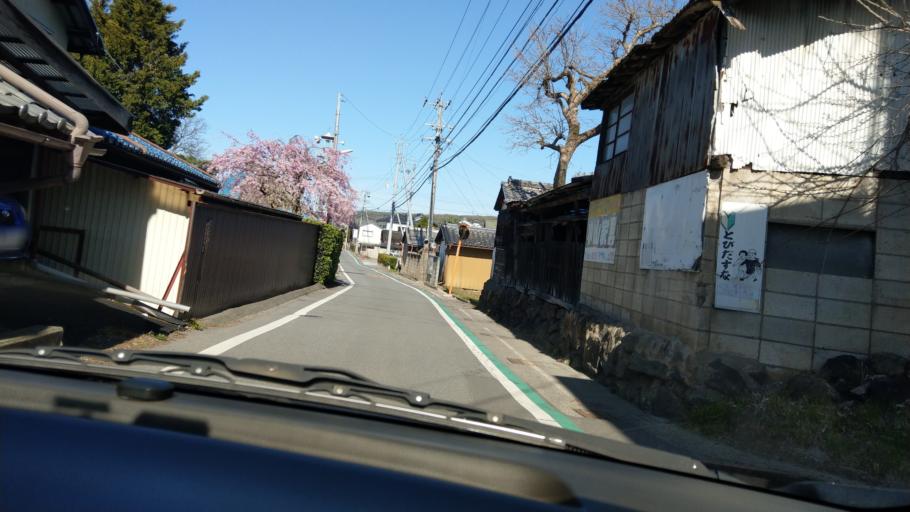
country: JP
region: Nagano
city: Komoro
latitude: 36.3350
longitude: 138.4932
